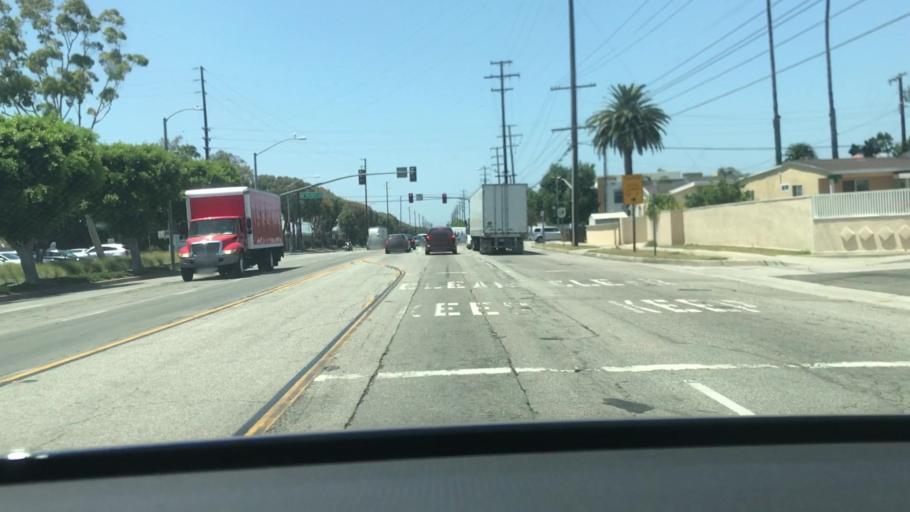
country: US
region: California
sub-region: Los Angeles County
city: Gardena
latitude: 33.8584
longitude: -118.3168
